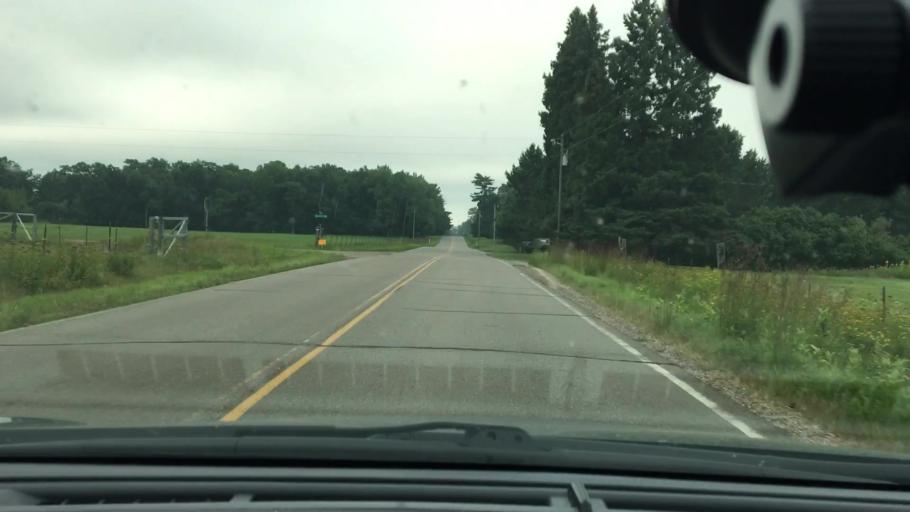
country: US
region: Minnesota
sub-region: Crow Wing County
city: Cross Lake
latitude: 46.6447
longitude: -94.0096
